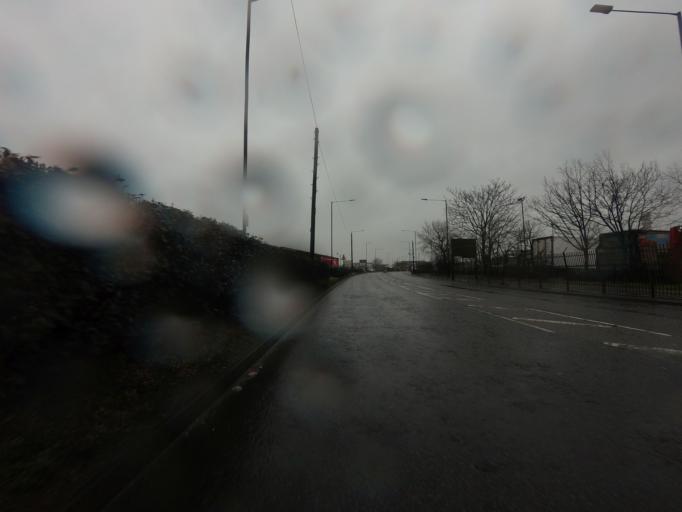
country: GB
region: England
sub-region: Hertfordshire
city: Waltham Cross
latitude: 51.6614
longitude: -0.0293
